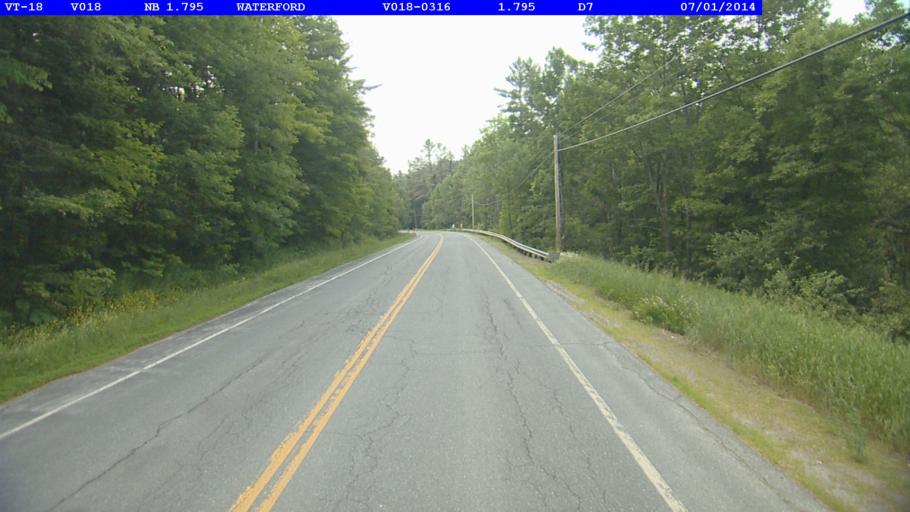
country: US
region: Vermont
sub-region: Caledonia County
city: Saint Johnsbury
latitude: 44.3628
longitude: -71.9049
